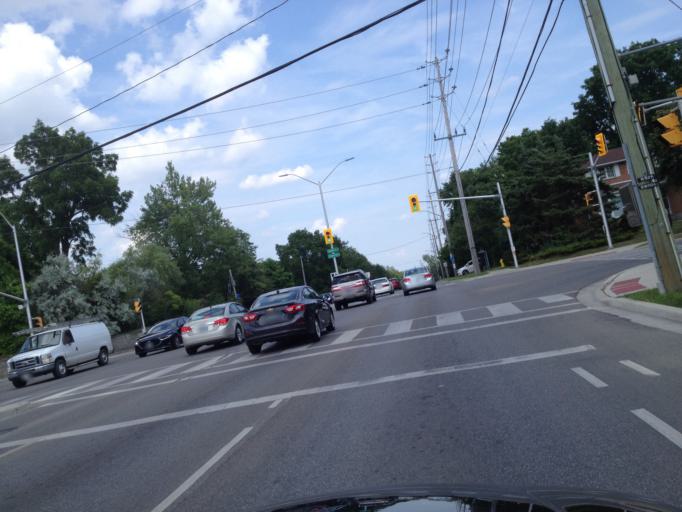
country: CA
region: Ontario
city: London
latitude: 42.9985
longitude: -81.2880
